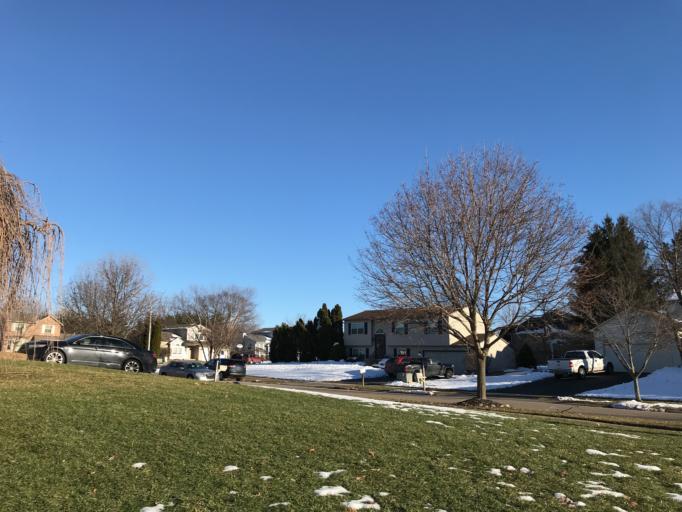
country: US
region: Michigan
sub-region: Oakland County
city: South Lyon
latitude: 42.4704
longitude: -83.6405
